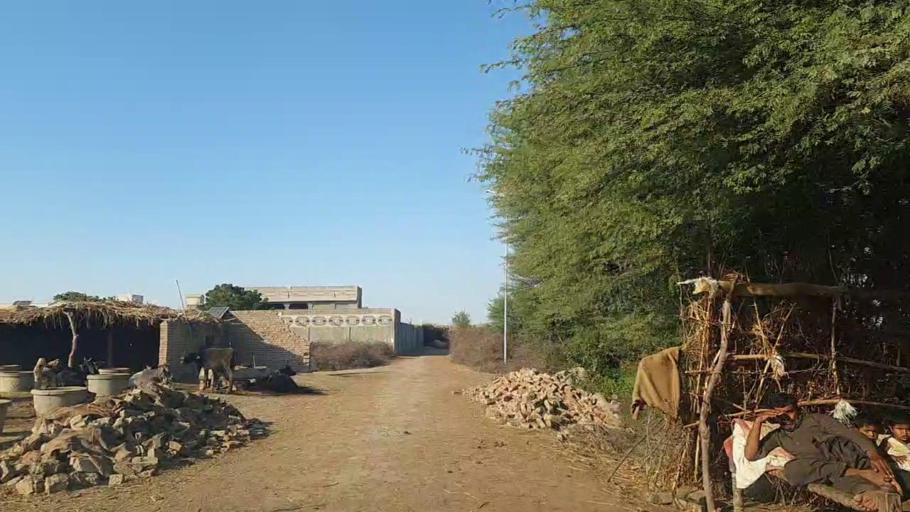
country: PK
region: Sindh
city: Shahpur Chakar
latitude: 26.1965
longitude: 68.6362
